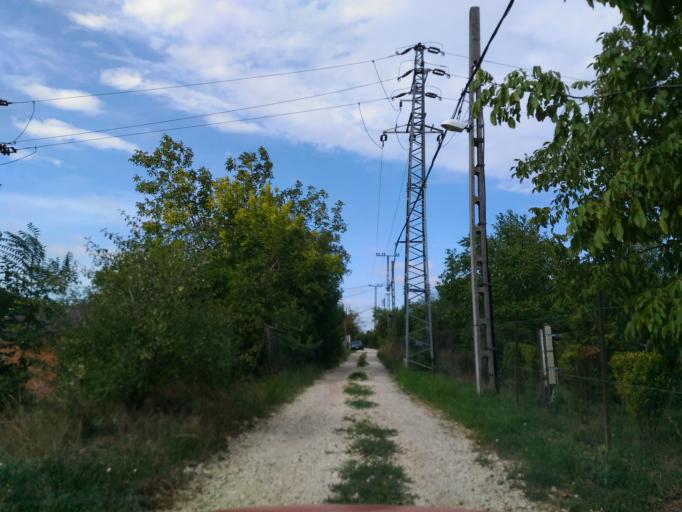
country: HU
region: Pest
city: Diosd
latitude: 47.4087
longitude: 18.9768
